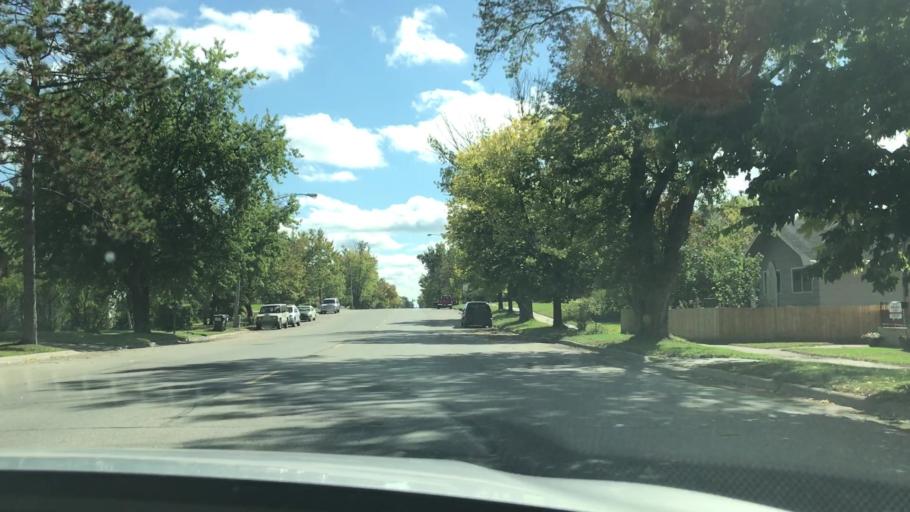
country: US
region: Minnesota
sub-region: Hubbard County
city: Park Rapids
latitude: 46.9266
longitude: -95.0585
